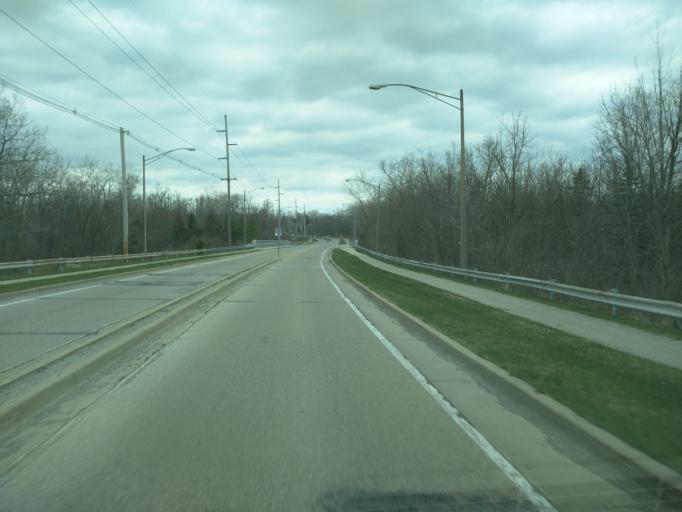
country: US
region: Michigan
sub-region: Ingham County
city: Lansing
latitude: 42.7176
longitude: -84.5224
